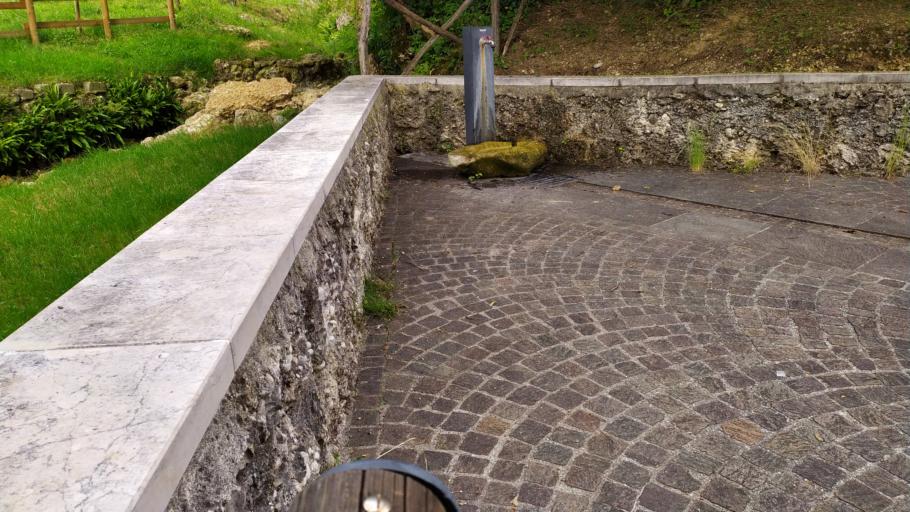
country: IT
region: Veneto
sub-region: Provincia di Treviso
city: Barbisano
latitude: 45.8727
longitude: 12.1981
